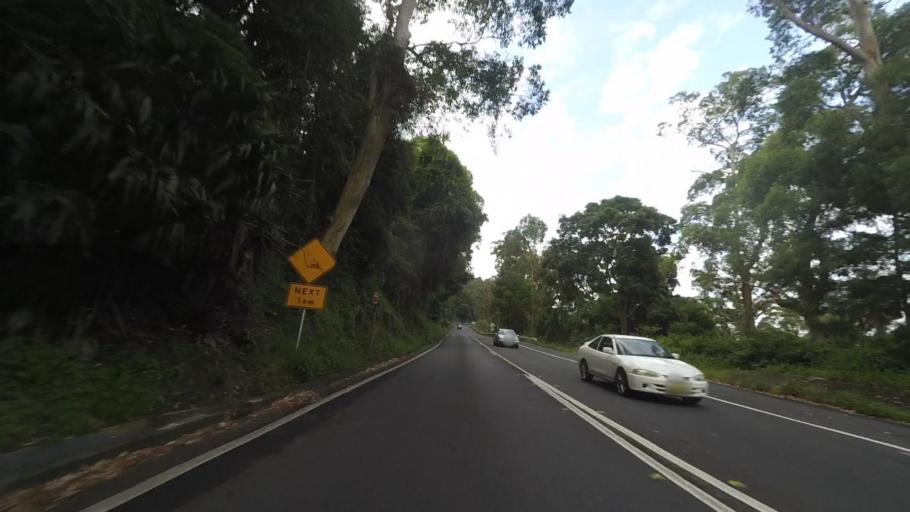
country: AU
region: New South Wales
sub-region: Wollongong
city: Bulli
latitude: -34.3215
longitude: 150.8943
